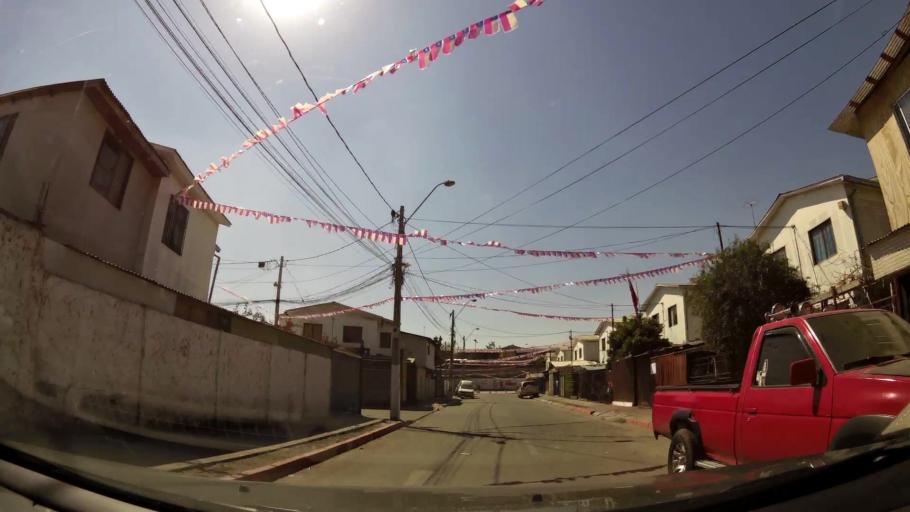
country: CL
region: Santiago Metropolitan
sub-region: Provincia de Cordillera
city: Puente Alto
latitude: -33.6275
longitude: -70.6086
